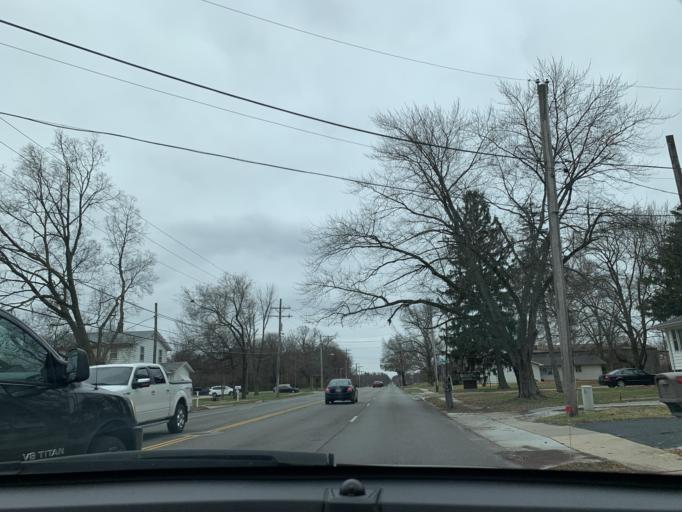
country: US
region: Illinois
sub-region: Sangamon County
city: Leland Grove
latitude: 39.8056
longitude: -89.6873
